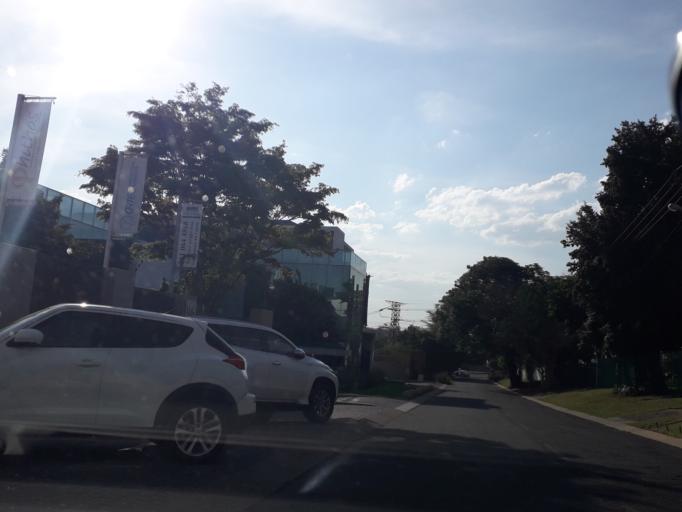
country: ZA
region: Gauteng
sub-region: City of Johannesburg Metropolitan Municipality
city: Johannesburg
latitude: -26.1008
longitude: 28.0391
